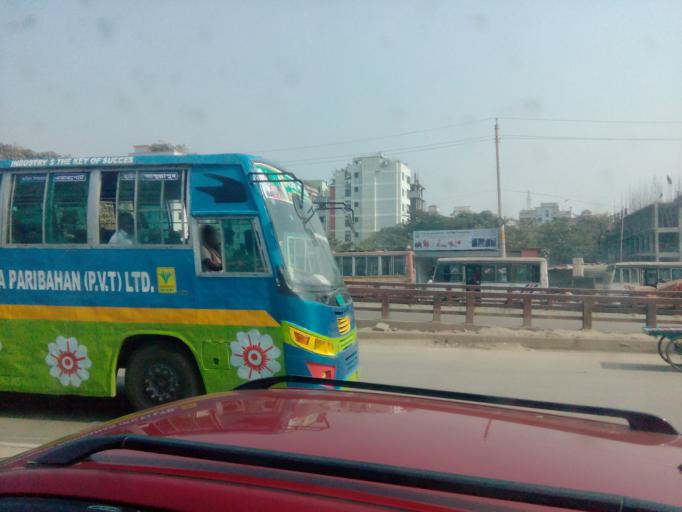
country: BD
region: Dhaka
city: Paltan
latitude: 23.7751
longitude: 90.4260
